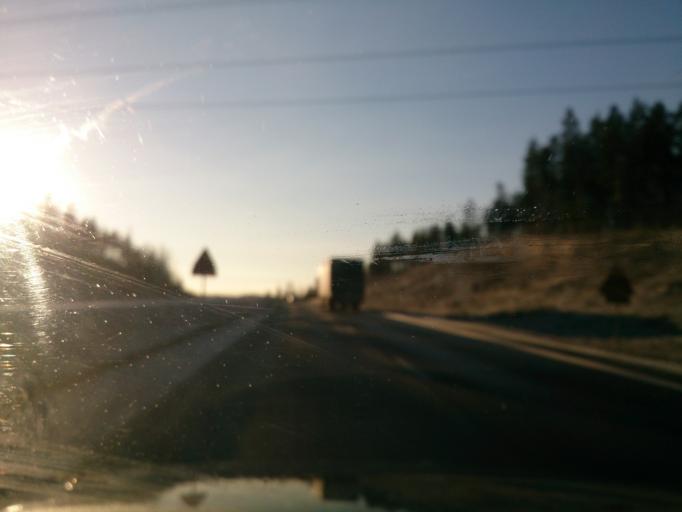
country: SE
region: OEstergoetland
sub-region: Norrkopings Kommun
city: Kimstad
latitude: 58.5155
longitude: 15.9961
